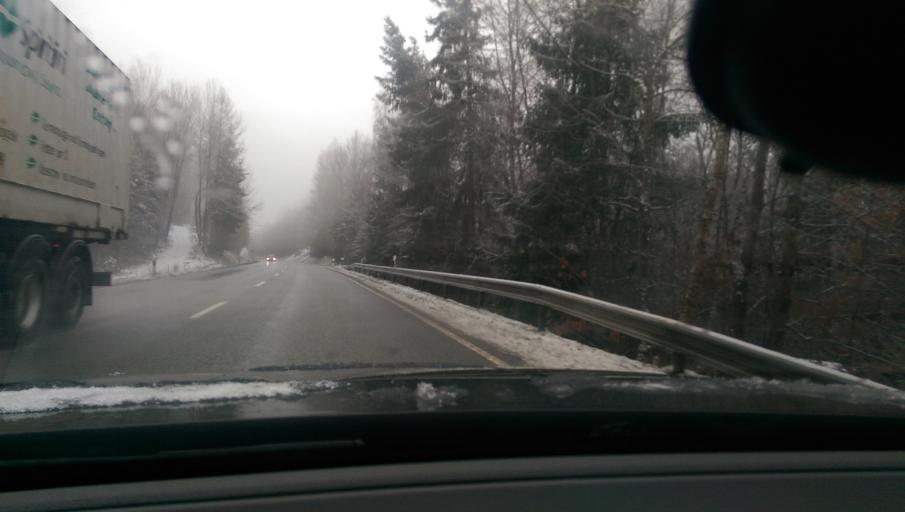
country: DE
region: Bavaria
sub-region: Lower Bavaria
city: Tiefenbach
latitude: 48.6034
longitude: 13.4096
